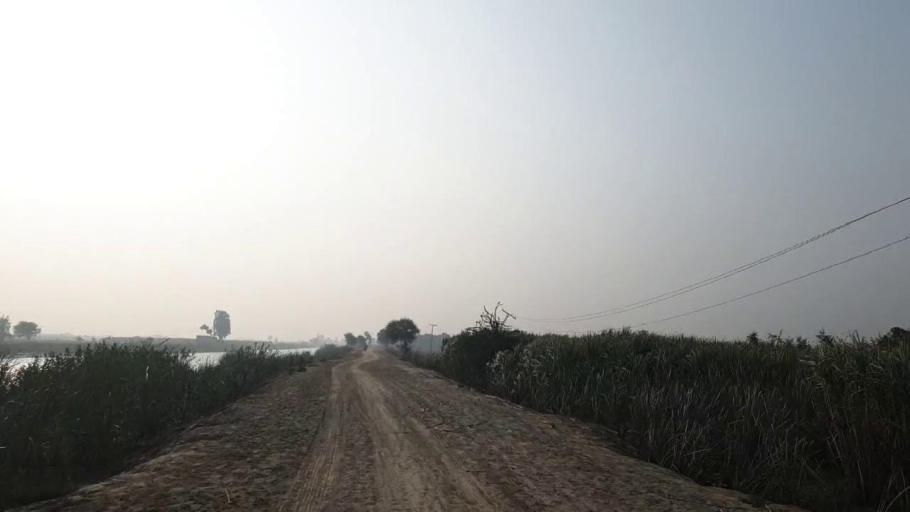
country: PK
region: Sindh
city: Tando Muhammad Khan
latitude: 25.1027
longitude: 68.5734
